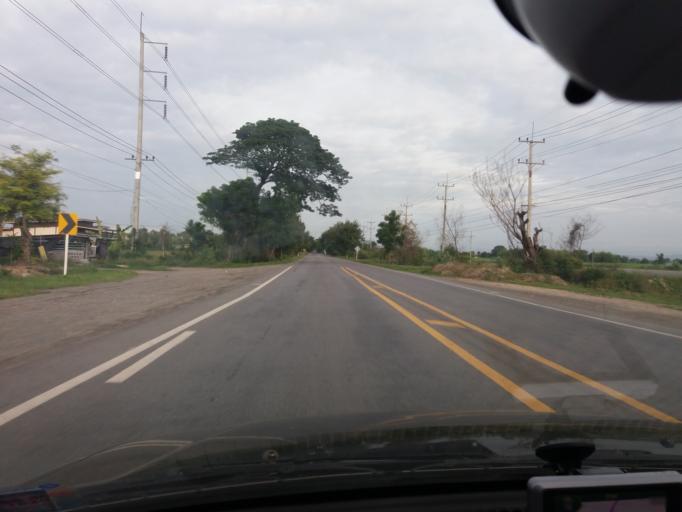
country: TH
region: Kanchanaburi
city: Huai Krachao
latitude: 14.3341
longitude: 99.7694
